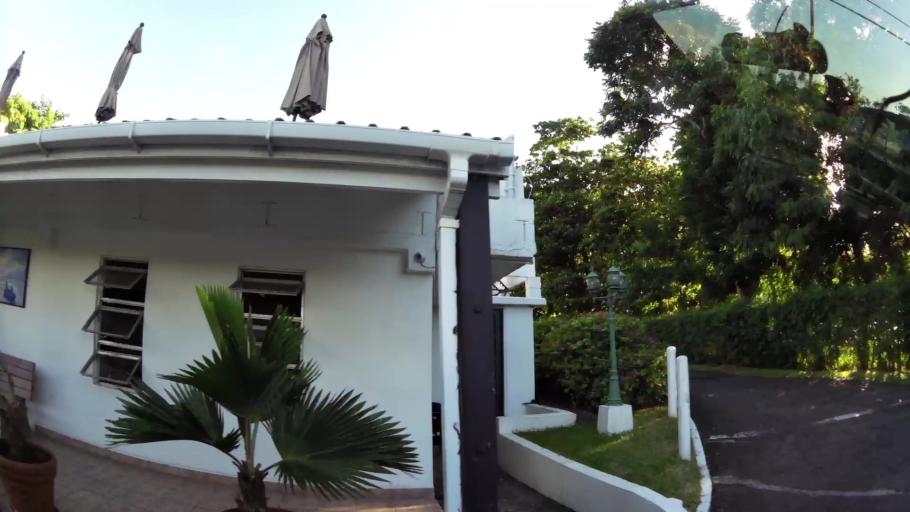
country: GD
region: Saint George
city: Saint George's
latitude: 12.0204
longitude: -61.7641
